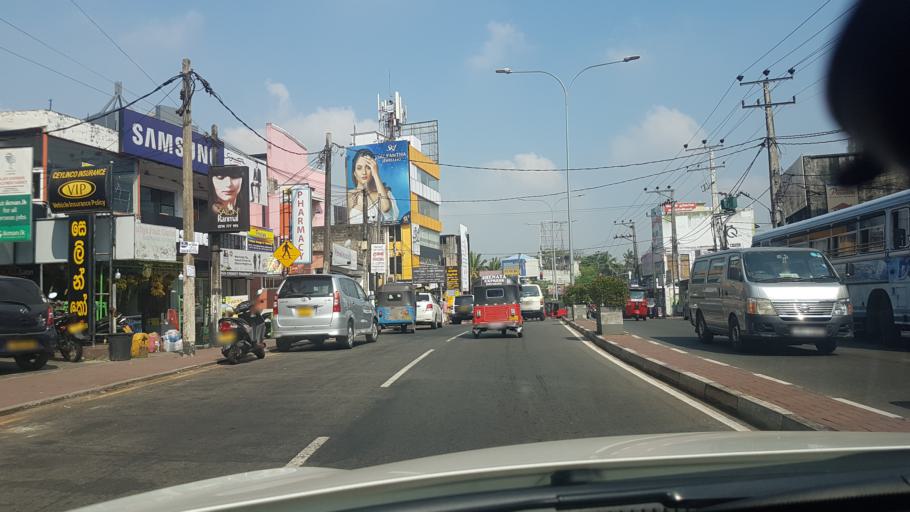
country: LK
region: Western
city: Battaramulla South
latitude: 6.9011
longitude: 79.9199
